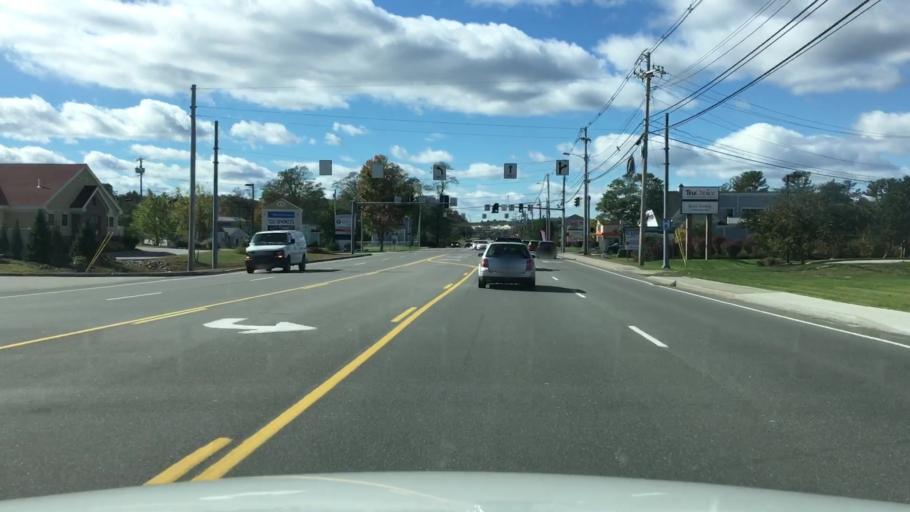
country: US
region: Maine
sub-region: York County
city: Biddeford
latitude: 43.4799
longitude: -70.4866
